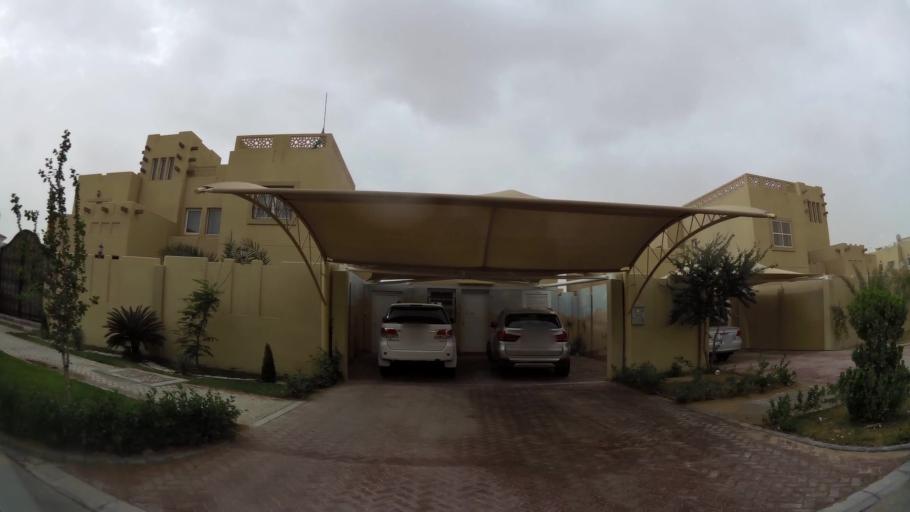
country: AE
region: Abu Dhabi
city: Abu Dhabi
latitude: 24.4549
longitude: 54.7187
